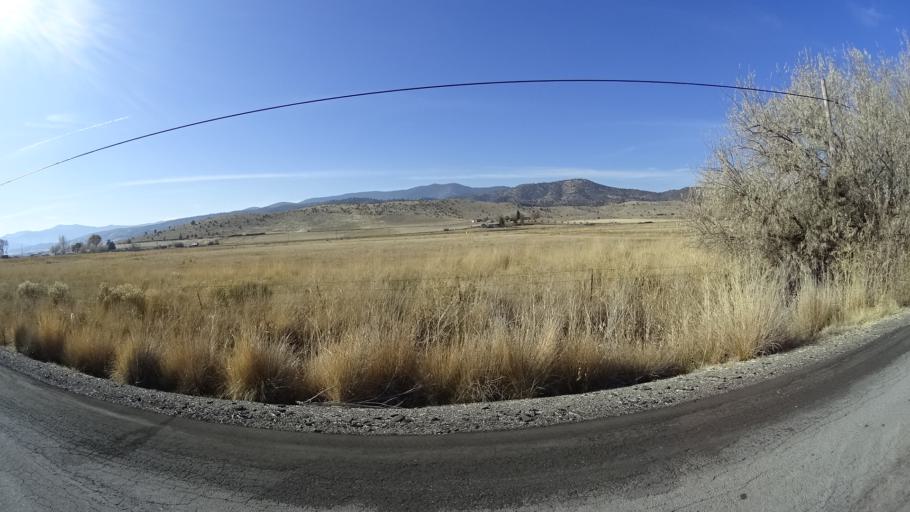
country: US
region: California
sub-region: Siskiyou County
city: Montague
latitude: 41.6068
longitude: -122.5233
